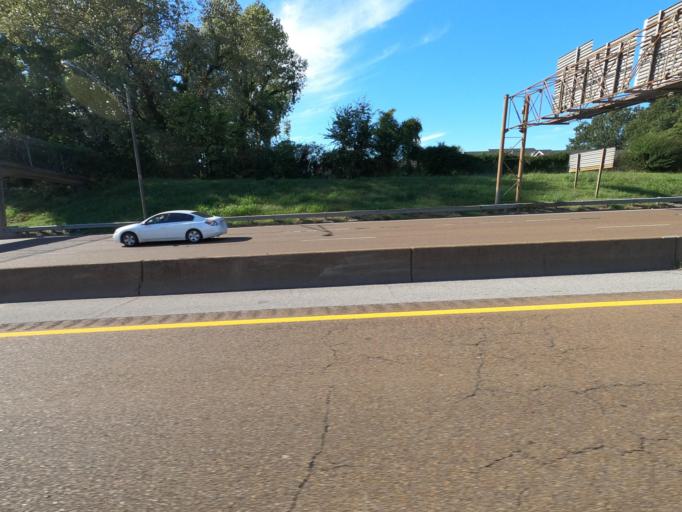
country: US
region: Tennessee
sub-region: Shelby County
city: Memphis
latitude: 35.1217
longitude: -90.0684
